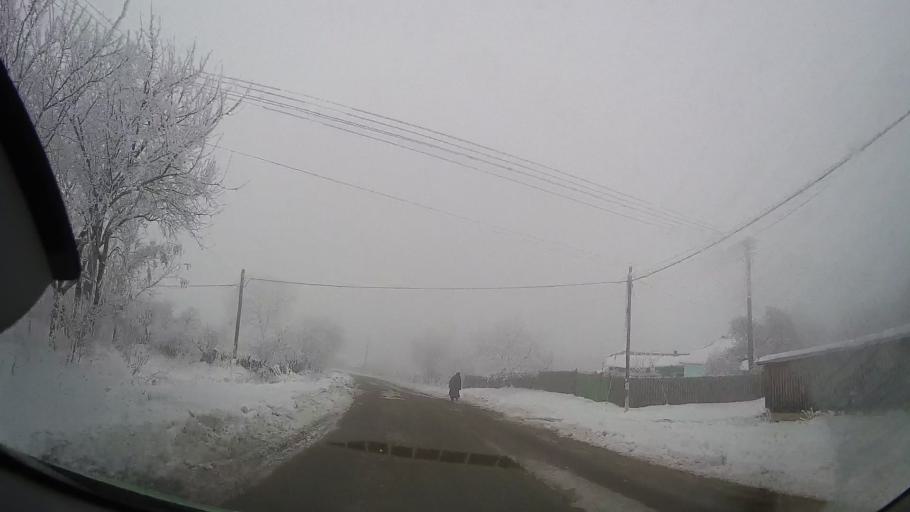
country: RO
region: Iasi
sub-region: Comuna Tansa
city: Suhulet
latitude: 46.9001
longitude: 27.2497
